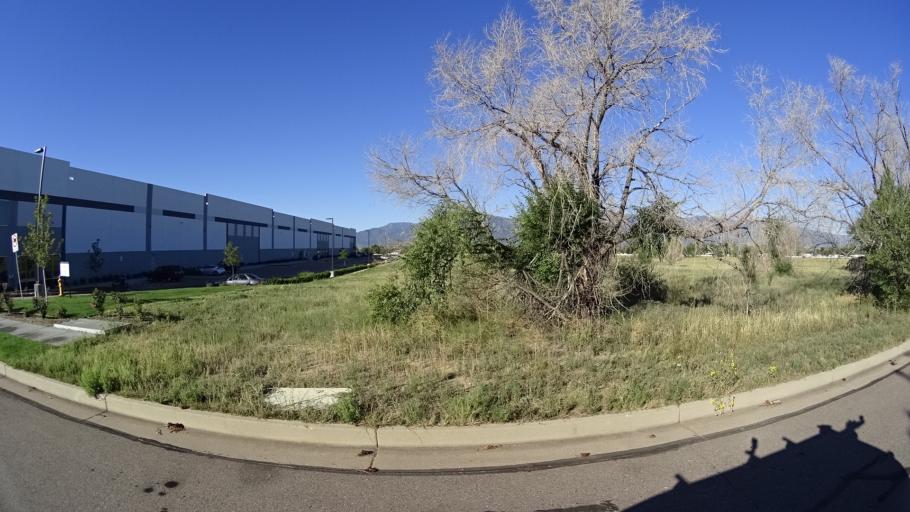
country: US
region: Colorado
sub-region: El Paso County
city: Security-Widefield
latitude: 38.7936
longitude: -104.7265
